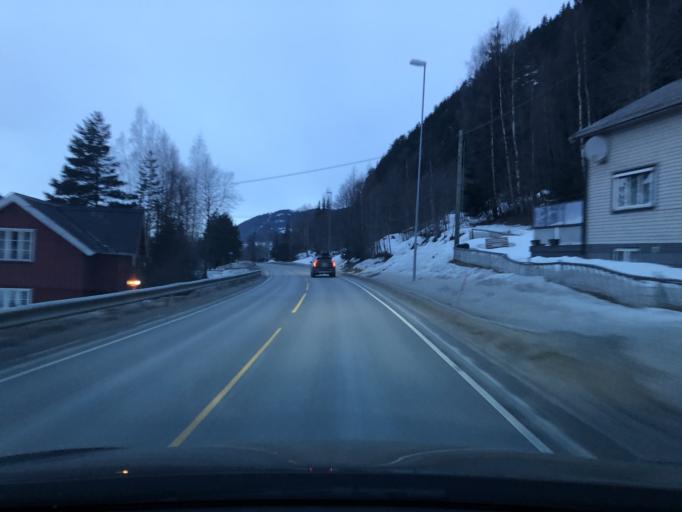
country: NO
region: Oppland
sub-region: Sor-Aurdal
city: Bagn
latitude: 60.9091
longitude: 9.4391
